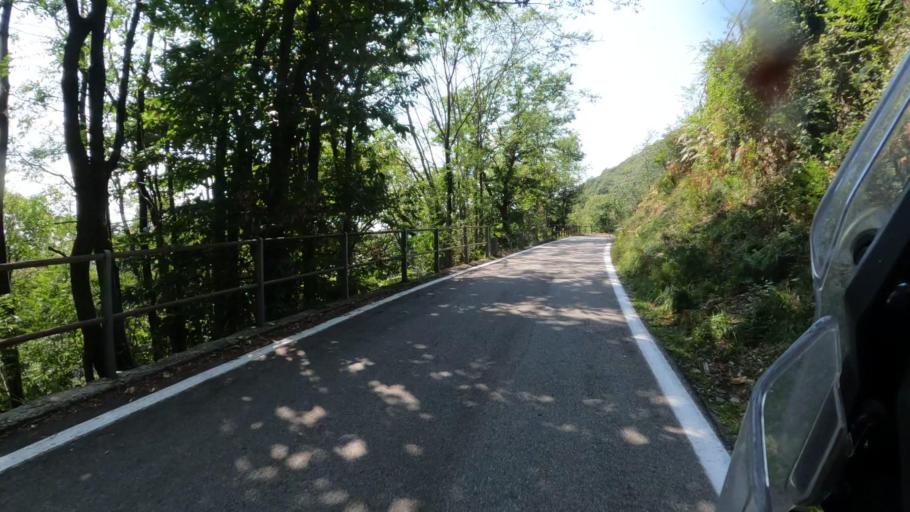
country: IT
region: Lombardy
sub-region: Provincia di Varese
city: Veddasca
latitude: 46.0594
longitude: 8.7773
